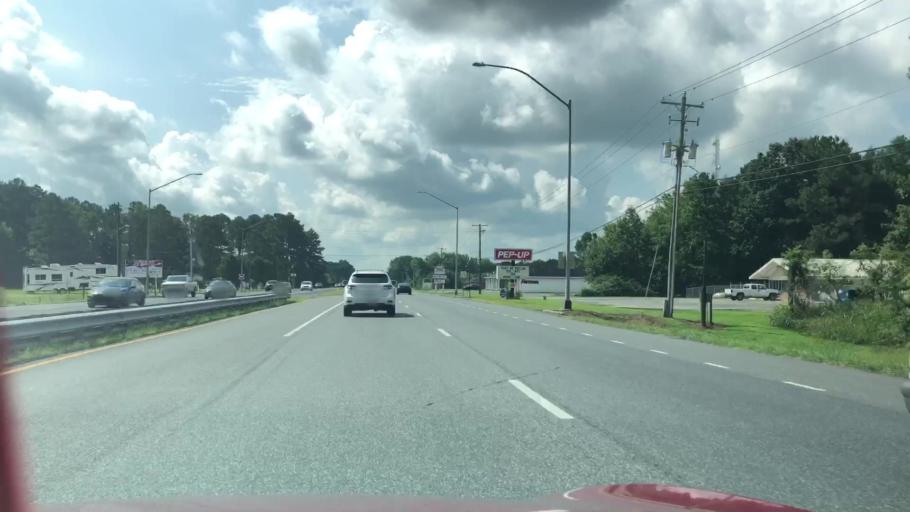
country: US
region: Maryland
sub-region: Worcester County
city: Pocomoke City
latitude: 38.0412
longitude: -75.5425
